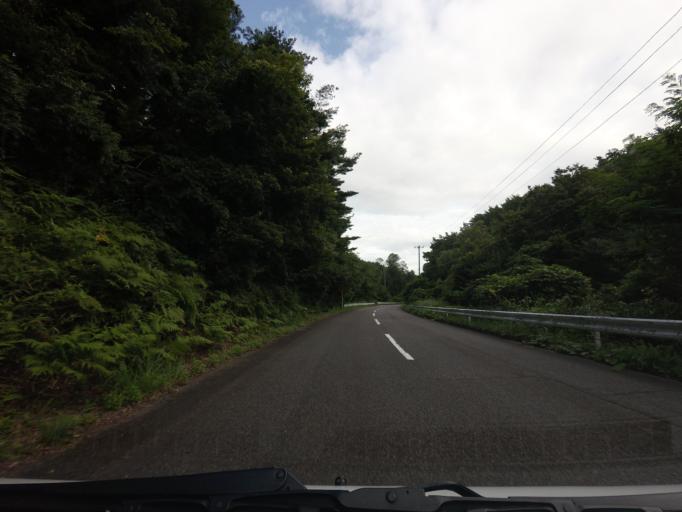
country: JP
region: Fukushima
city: Motomiya
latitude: 37.5448
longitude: 140.3203
